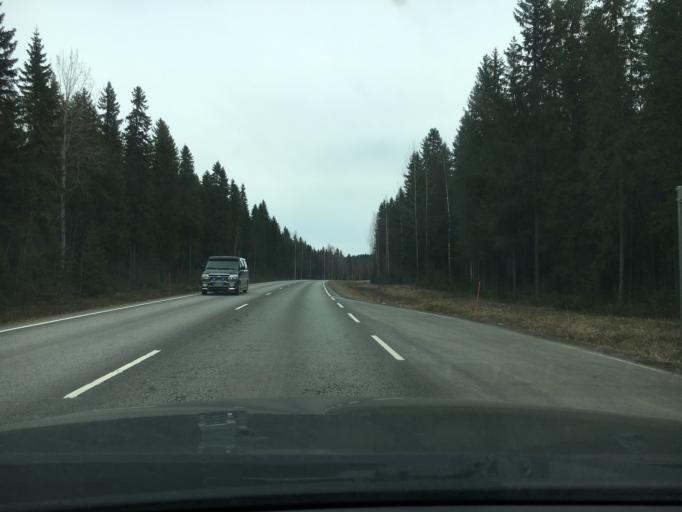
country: FI
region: Central Finland
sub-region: AEaenekoski
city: Konnevesi
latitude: 62.6119
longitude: 26.2440
